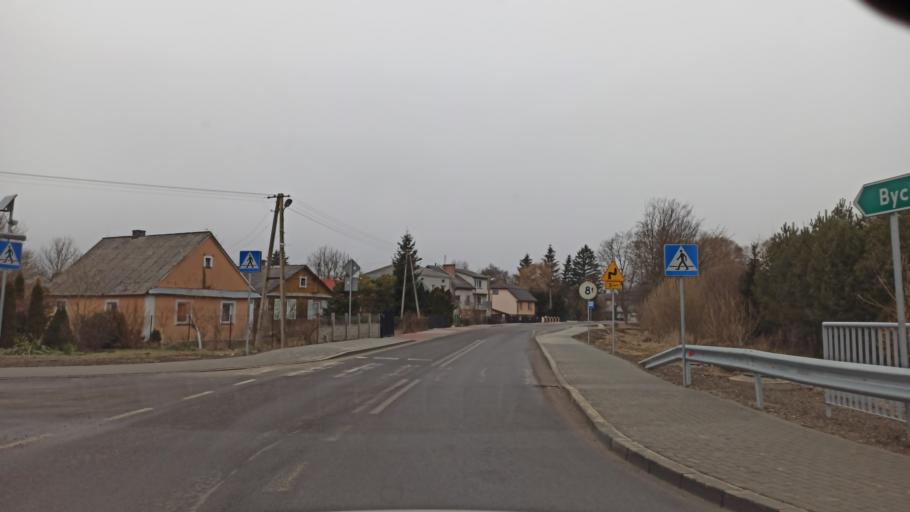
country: PL
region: Lublin Voivodeship
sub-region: Powiat lubelski
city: Wysokie
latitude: 50.9092
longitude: 22.6625
